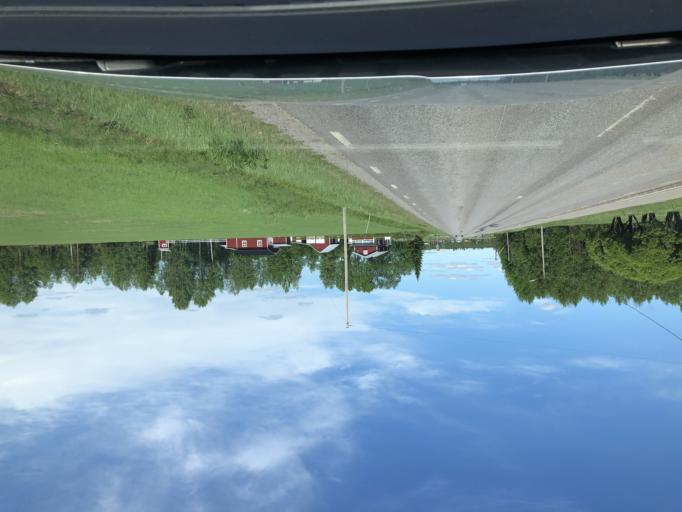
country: SE
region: Norrbotten
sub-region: Pitea Kommun
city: Roknas
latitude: 65.4333
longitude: 21.2742
